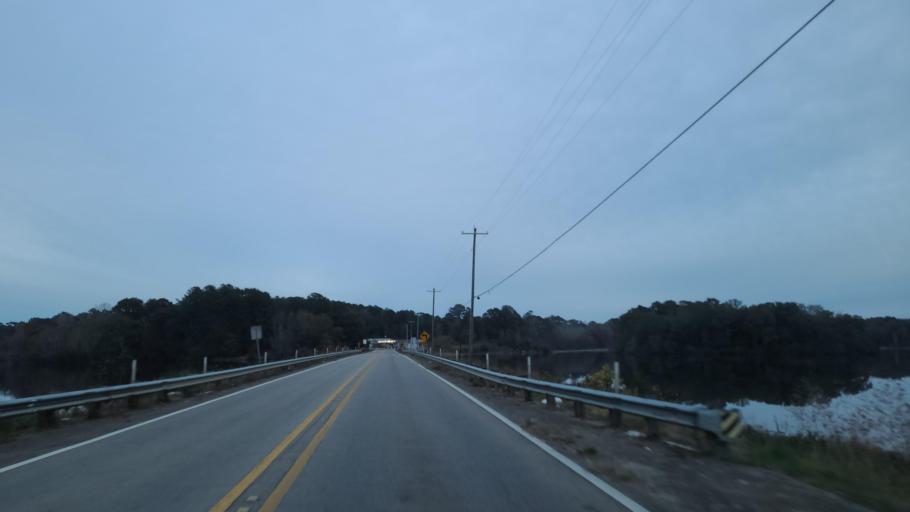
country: US
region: Mississippi
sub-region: Clarke County
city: Quitman
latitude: 32.0394
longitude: -88.7126
